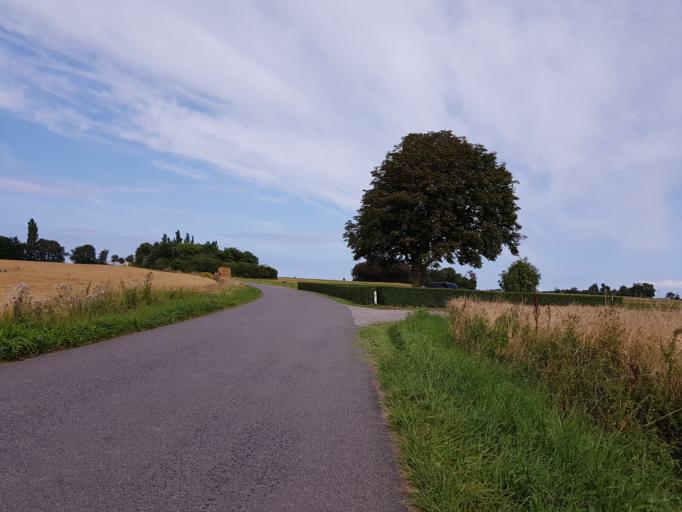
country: DK
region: Zealand
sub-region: Guldborgsund Kommune
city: Nykobing Falster
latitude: 54.5817
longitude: 11.9429
